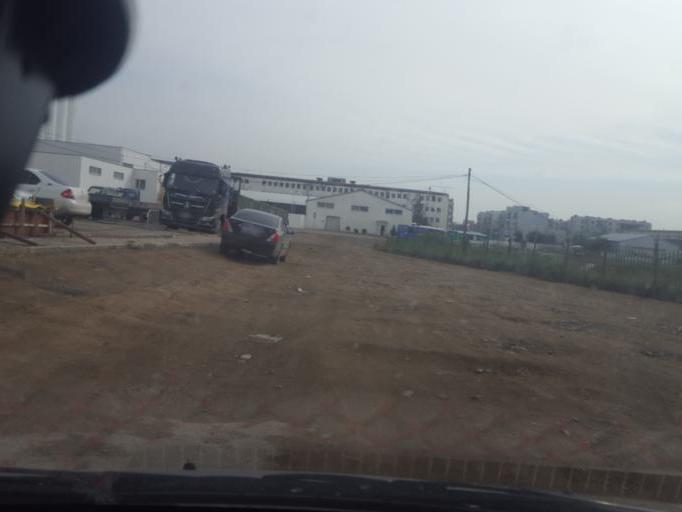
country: MN
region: Ulaanbaatar
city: Ulaanbaatar
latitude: 47.9149
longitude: 106.8023
